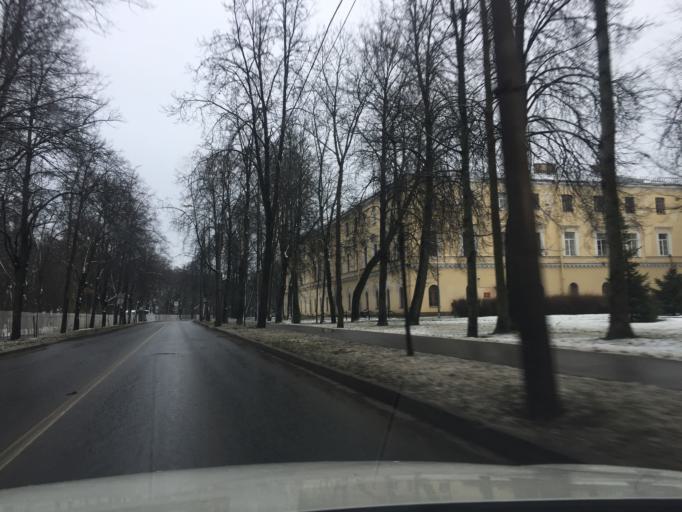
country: RU
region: St.-Petersburg
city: Pushkin
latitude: 59.7098
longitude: 30.3994
